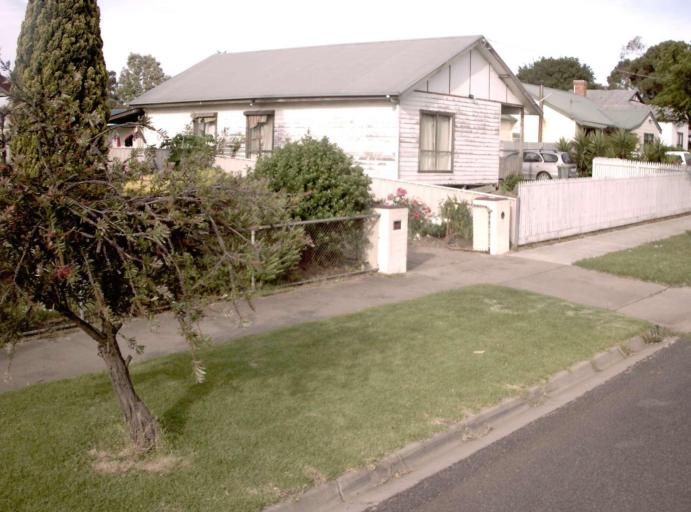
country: AU
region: Victoria
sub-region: Wellington
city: Heyfield
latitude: -37.9790
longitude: 146.7887
